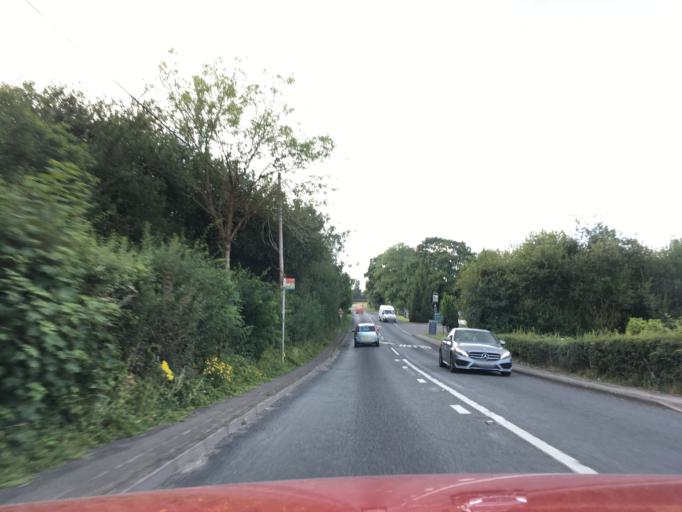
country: GB
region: England
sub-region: Hampshire
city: Swanmore
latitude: 50.9275
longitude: -1.2012
